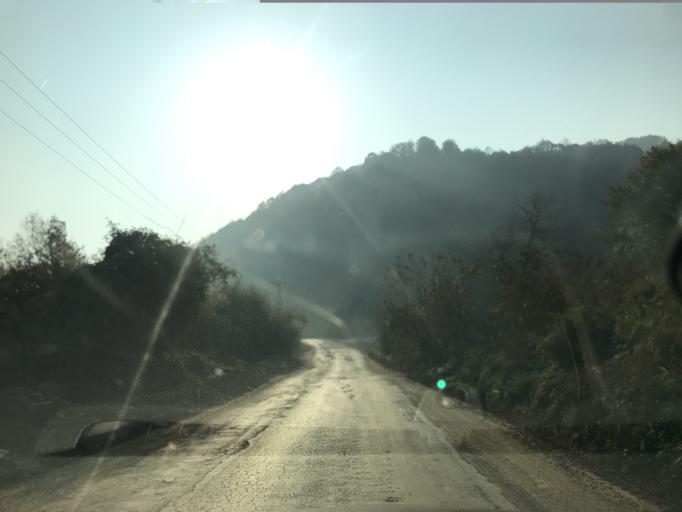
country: TR
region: Duzce
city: Cumayeri
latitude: 40.9194
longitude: 30.9297
